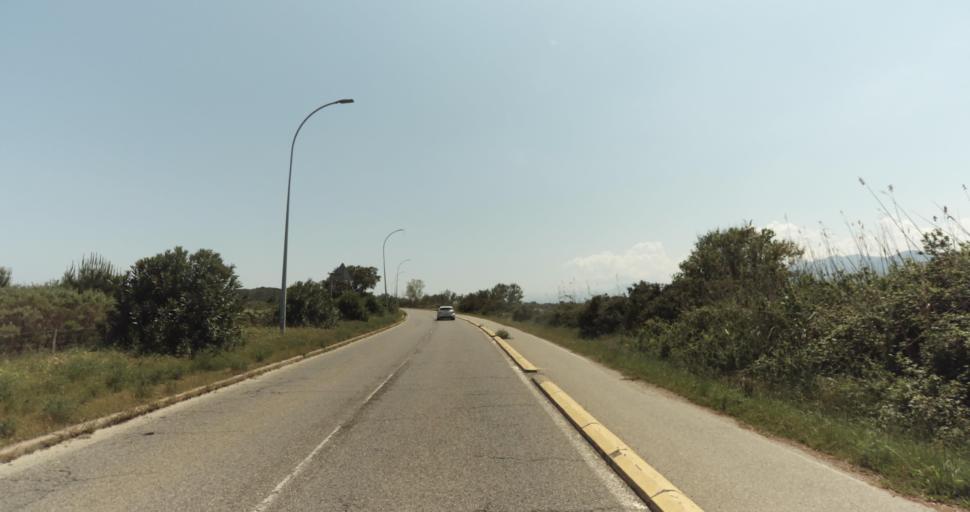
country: FR
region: Corsica
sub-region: Departement de la Haute-Corse
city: Biguglia
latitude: 42.6531
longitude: 9.4504
